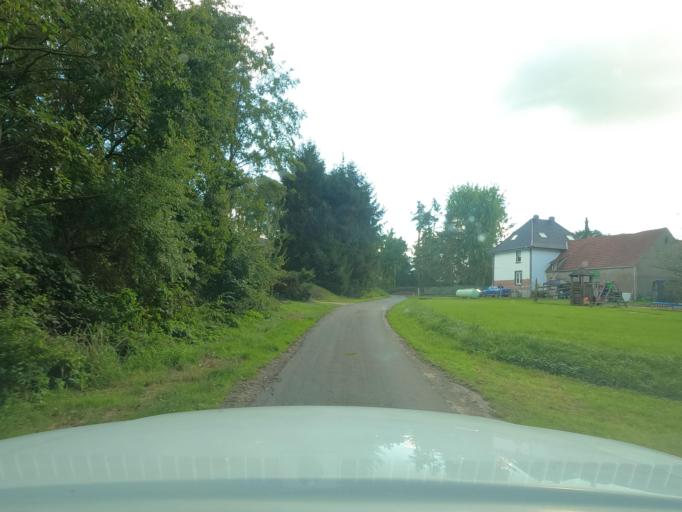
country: DE
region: North Rhine-Westphalia
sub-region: Regierungsbezirk Dusseldorf
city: Hunxe
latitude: 51.6575
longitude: 6.7995
